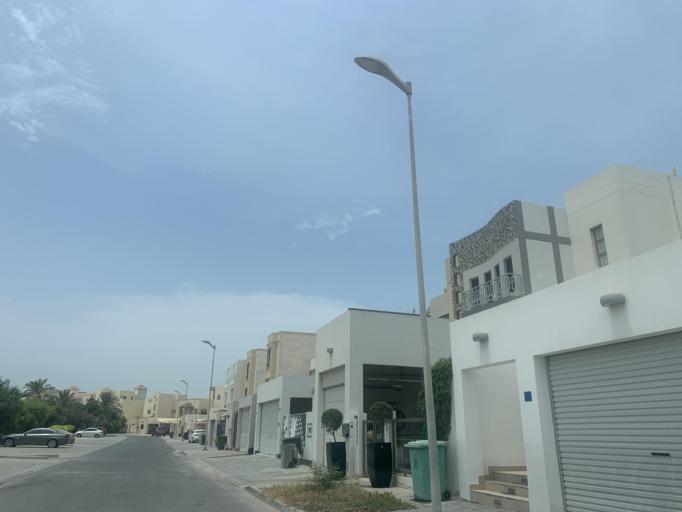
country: BH
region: Muharraq
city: Al Hadd
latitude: 26.2944
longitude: 50.6628
